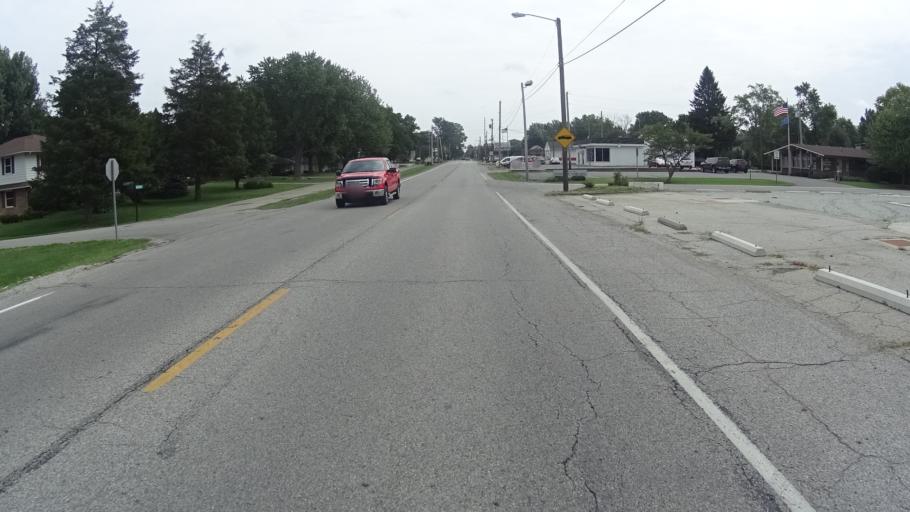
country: US
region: Indiana
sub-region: Madison County
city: Edgewood
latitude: 40.1015
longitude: -85.7331
